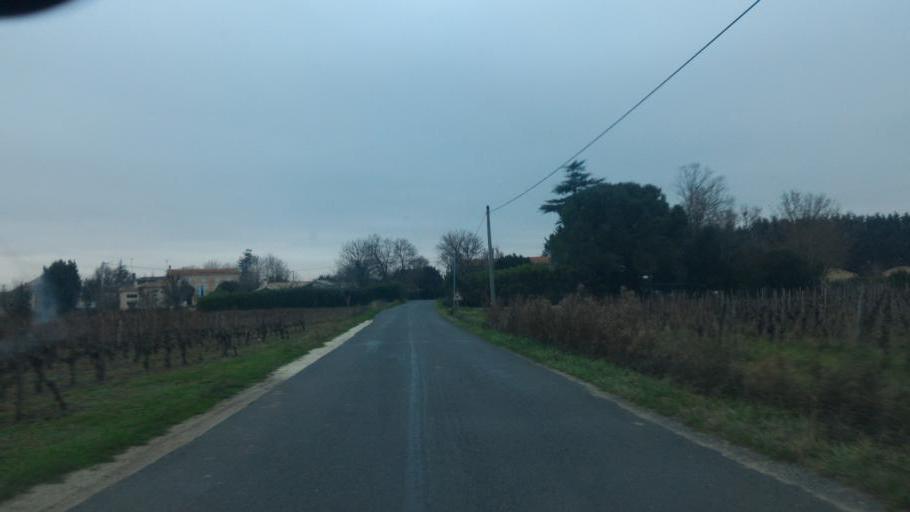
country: FR
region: Aquitaine
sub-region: Departement de la Gironde
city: Cars
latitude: 45.1405
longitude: -0.6291
